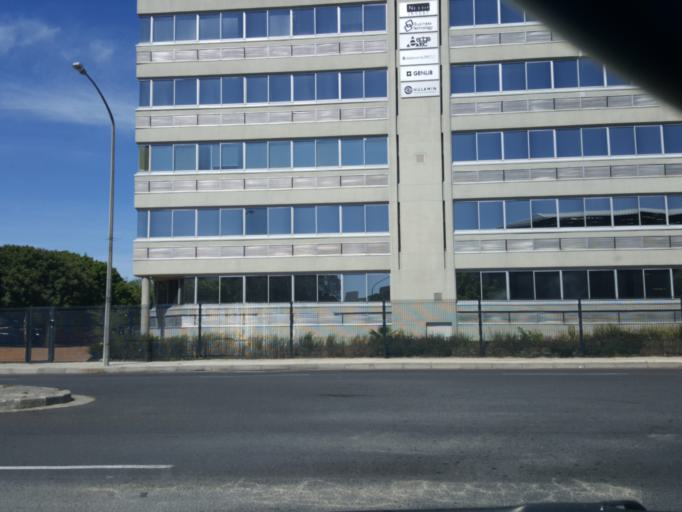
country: ZA
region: Western Cape
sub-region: City of Cape Town
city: Rosebank
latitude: -33.9338
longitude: 18.5094
